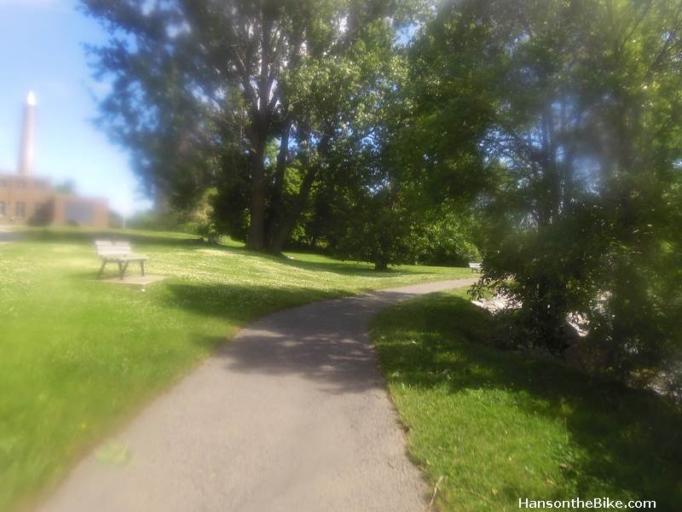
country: CA
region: Ontario
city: Kingston
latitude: 44.2160
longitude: -76.5207
